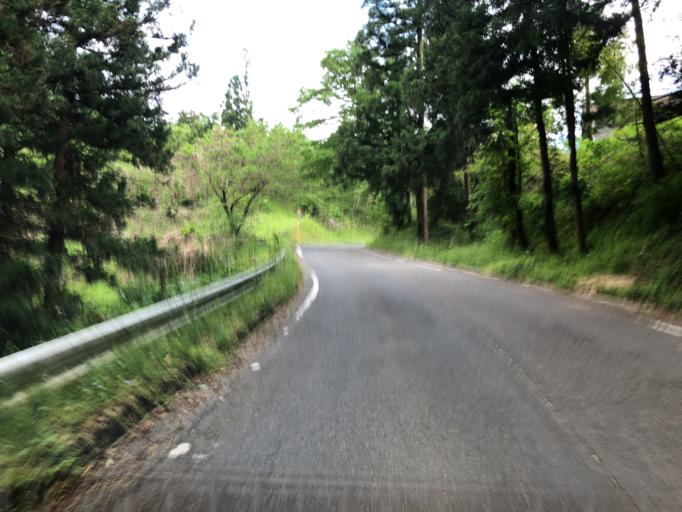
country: JP
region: Fukushima
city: Nihommatsu
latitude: 37.6320
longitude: 140.5064
